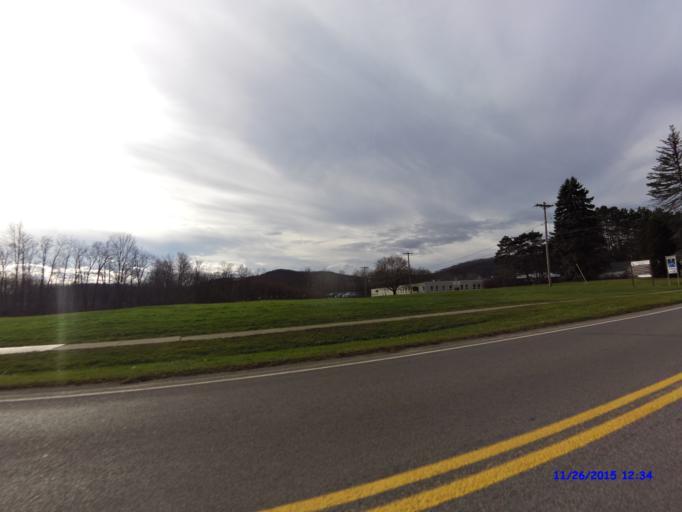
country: US
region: New York
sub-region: Cattaraugus County
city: Allegany
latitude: 42.0841
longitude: -78.4874
